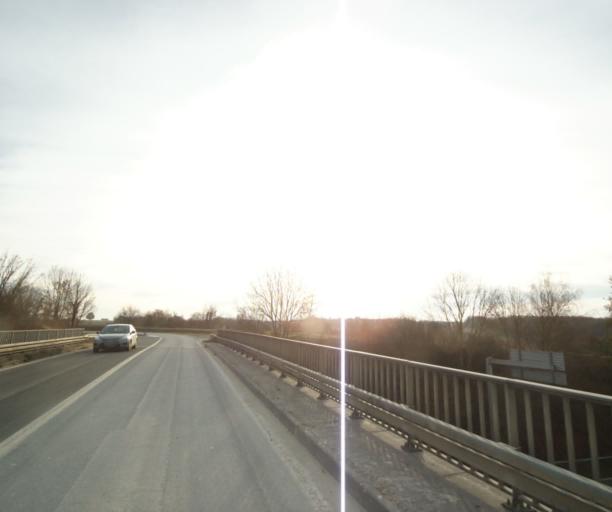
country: FR
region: Poitou-Charentes
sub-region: Departement de la Charente-Maritime
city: Saint-Porchaire
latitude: 45.8117
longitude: -0.7682
